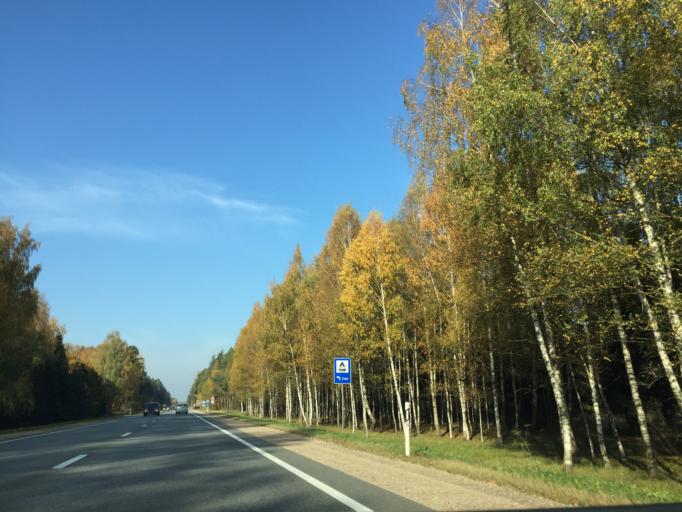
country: LV
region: Babite
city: Pinki
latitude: 56.8836
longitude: 23.9460
